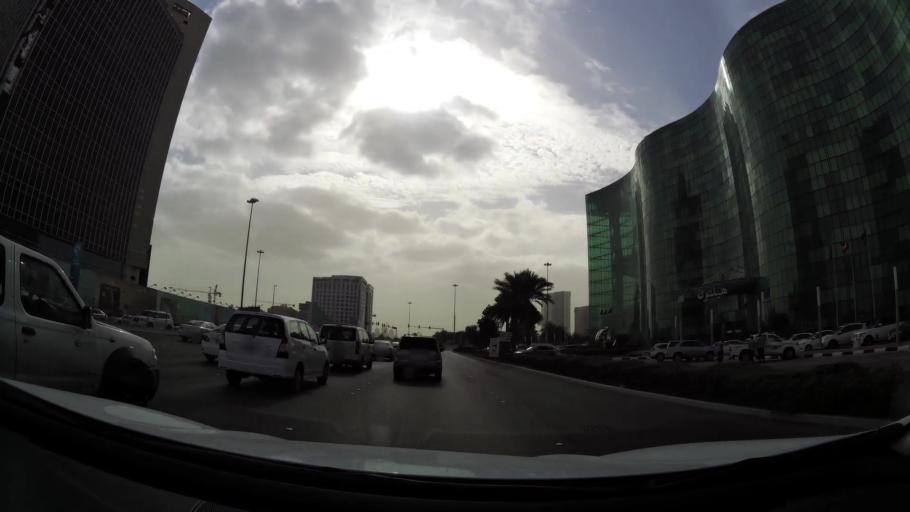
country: AE
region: Abu Dhabi
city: Abu Dhabi
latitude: 24.4222
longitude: 54.4568
